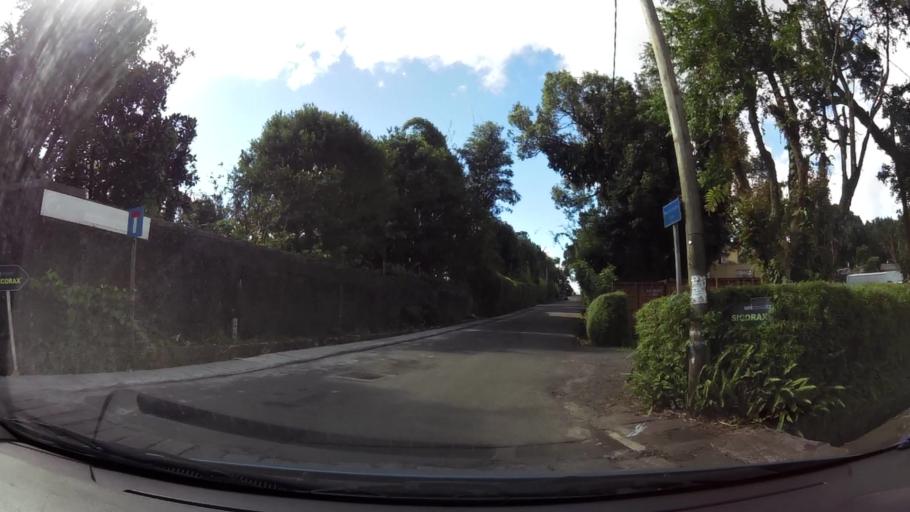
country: MU
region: Plaines Wilhems
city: Curepipe
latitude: -20.3230
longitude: 57.5329
